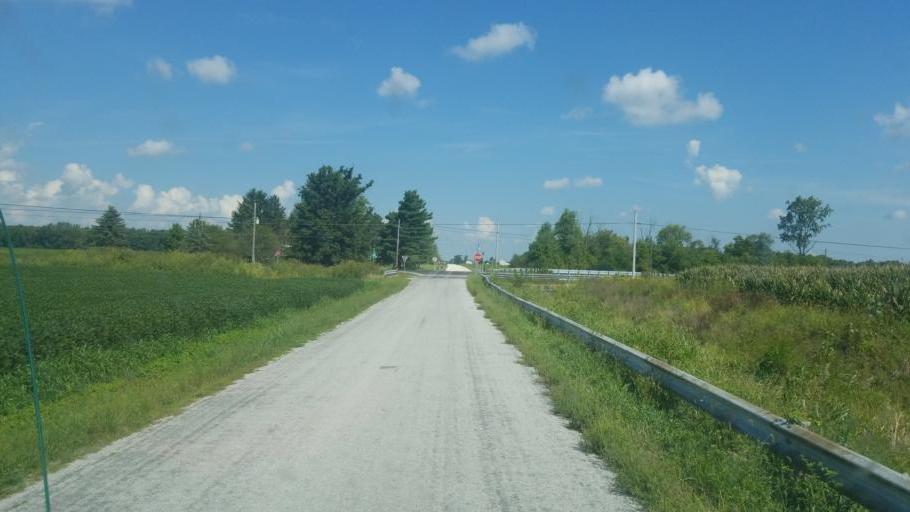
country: US
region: Ohio
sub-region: Hardin County
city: Forest
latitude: 40.6861
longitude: -83.4957
